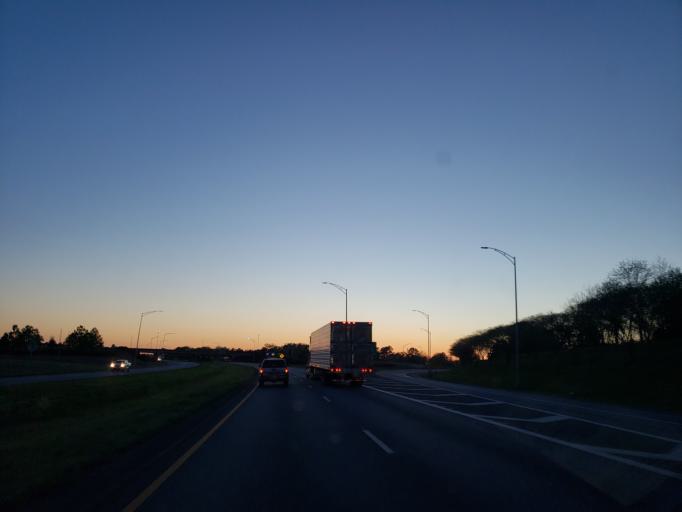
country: US
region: Alabama
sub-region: Tuscaloosa County
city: Tuscaloosa
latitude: 33.1713
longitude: -87.5483
